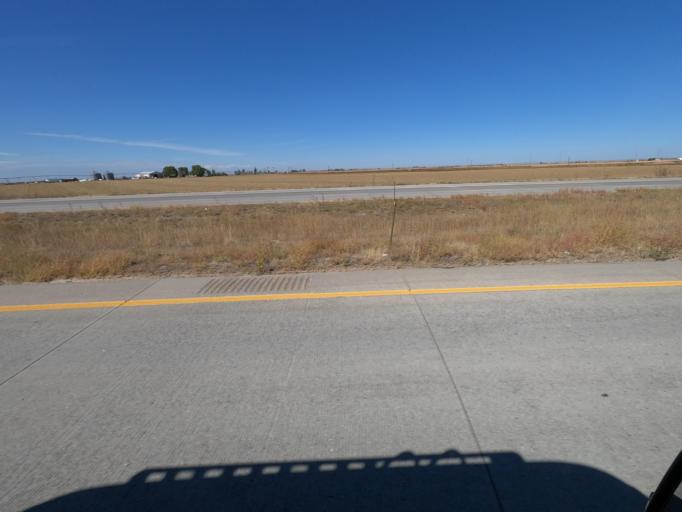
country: US
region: Colorado
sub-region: Morgan County
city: Fort Morgan
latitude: 40.2451
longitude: -104.0626
